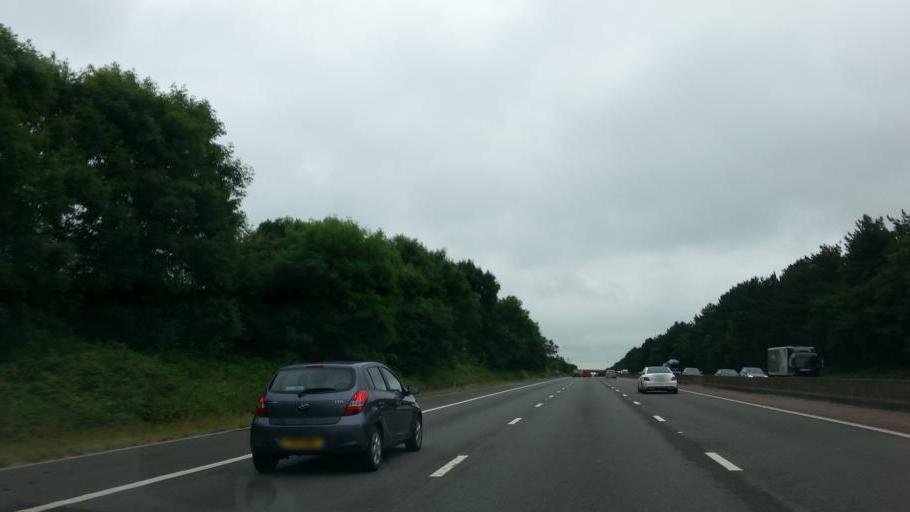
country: GB
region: England
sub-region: Leicestershire
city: Lutterworth
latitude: 52.4838
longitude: -1.1919
